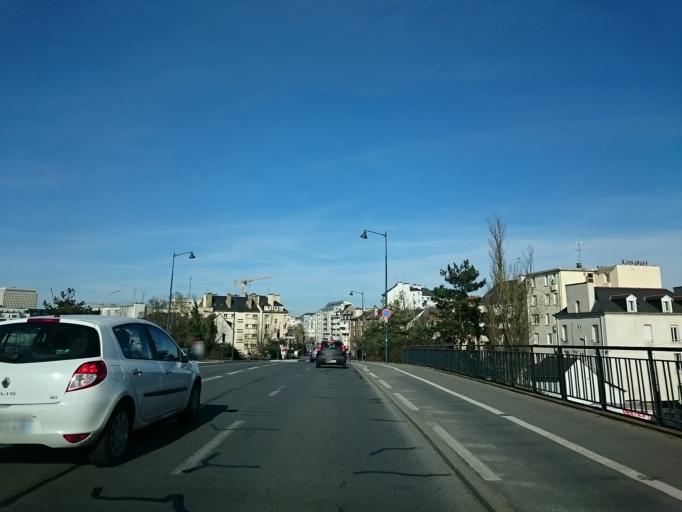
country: FR
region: Brittany
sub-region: Departement d'Ille-et-Vilaine
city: Rennes
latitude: 48.1045
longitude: -1.6640
